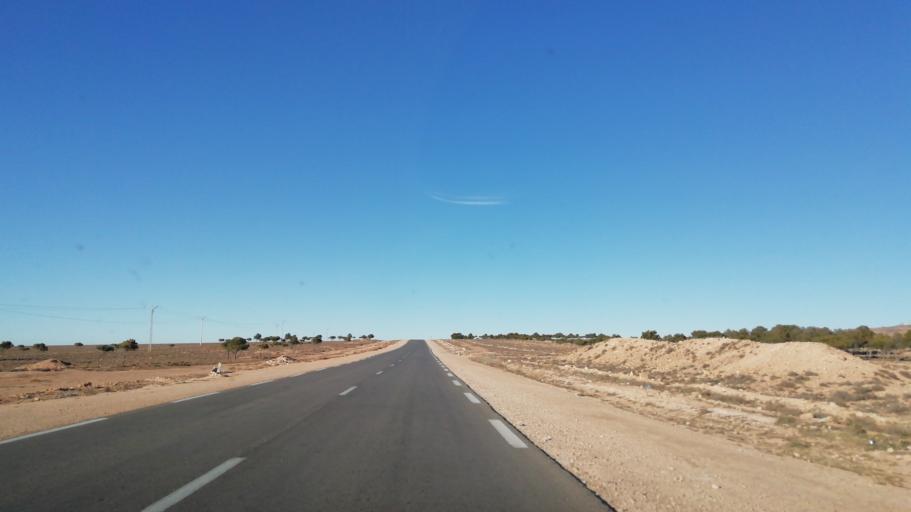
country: DZ
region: Tlemcen
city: Sebdou
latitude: 34.2549
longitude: -1.2576
